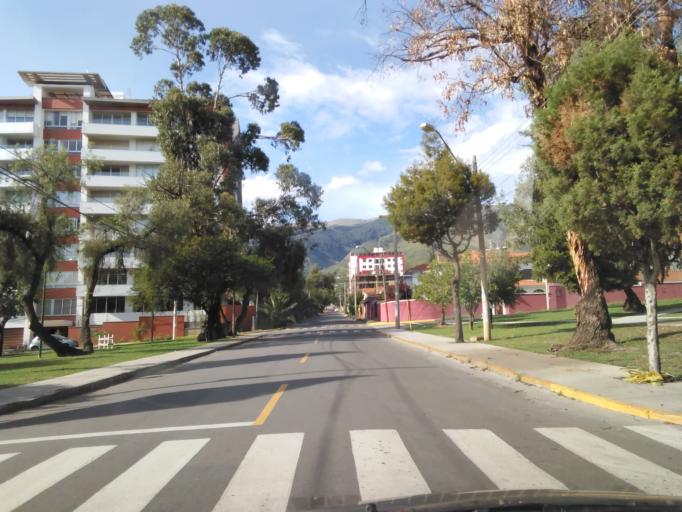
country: BO
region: Cochabamba
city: Cochabamba
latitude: -17.3715
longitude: -66.1464
